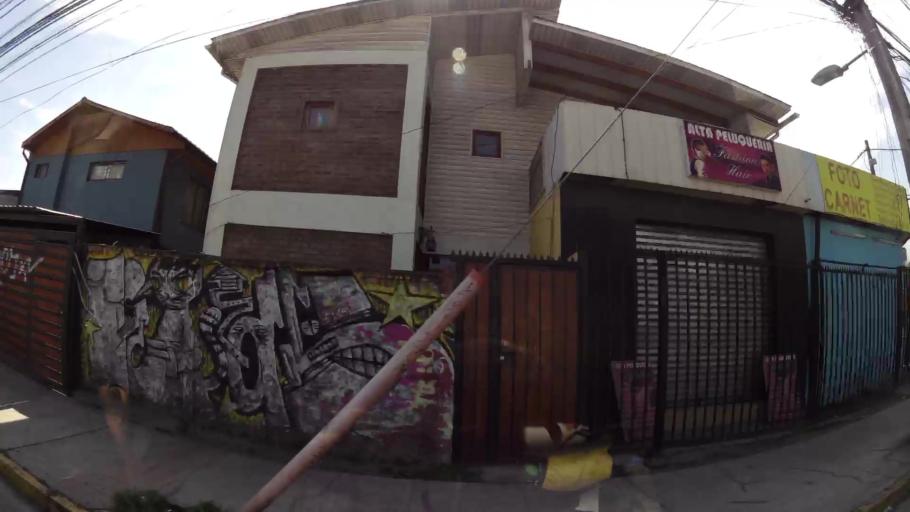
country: CL
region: Santiago Metropolitan
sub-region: Provincia de Santiago
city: Villa Presidente Frei, Nunoa, Santiago, Chile
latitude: -33.4712
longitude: -70.5437
